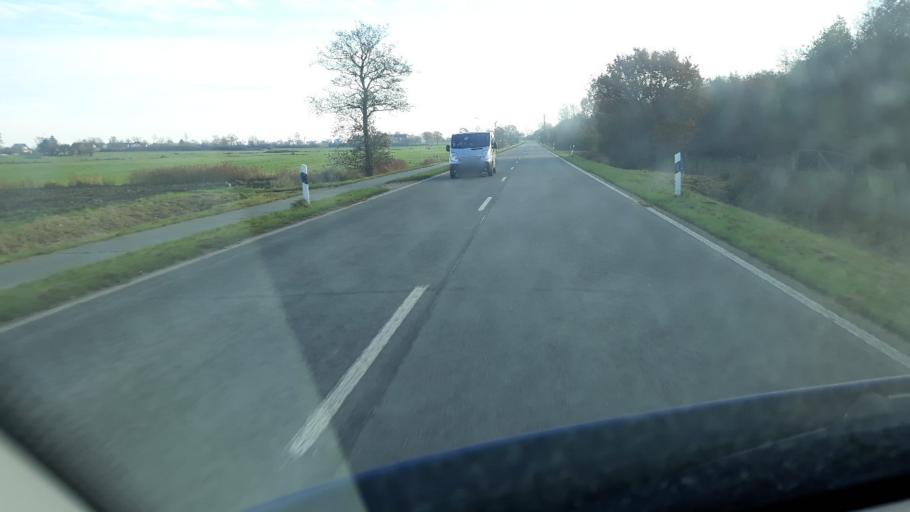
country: DE
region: Schleswig-Holstein
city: Maasholm
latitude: 54.6609
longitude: 9.9955
